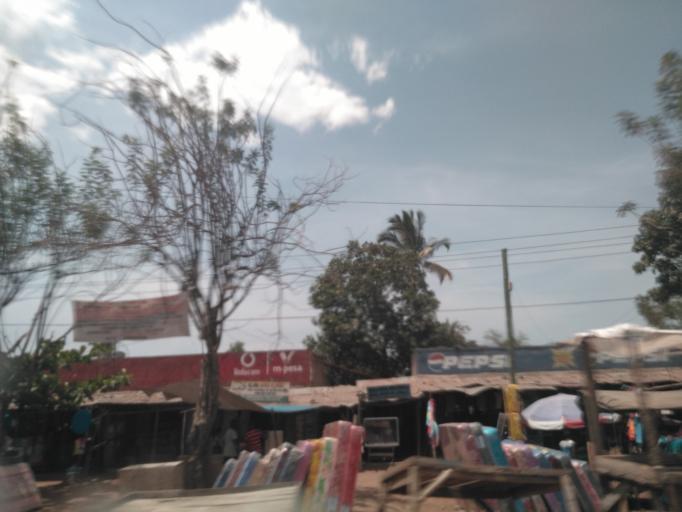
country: TZ
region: Mwanza
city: Mwanza
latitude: -2.5444
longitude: 32.9801
